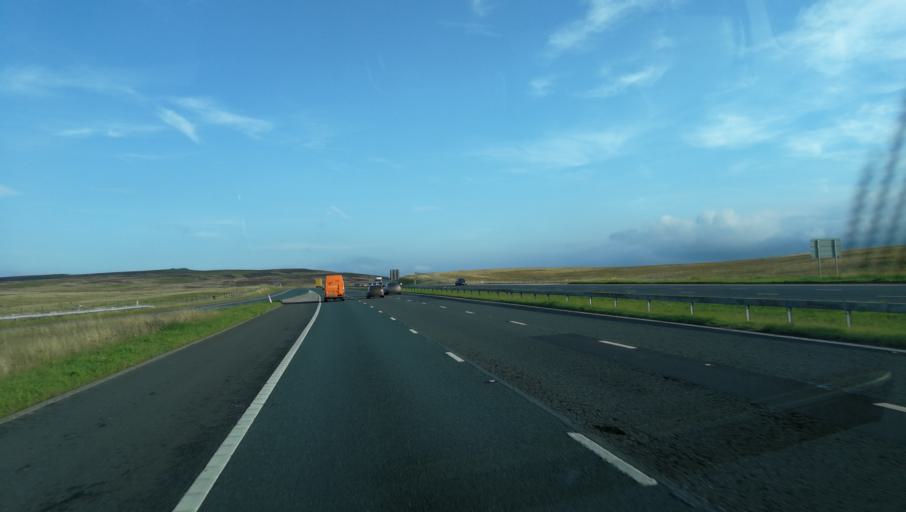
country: GB
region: England
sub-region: Cumbria
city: Appleby-in-Westmorland
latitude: 54.5067
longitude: -2.6485
